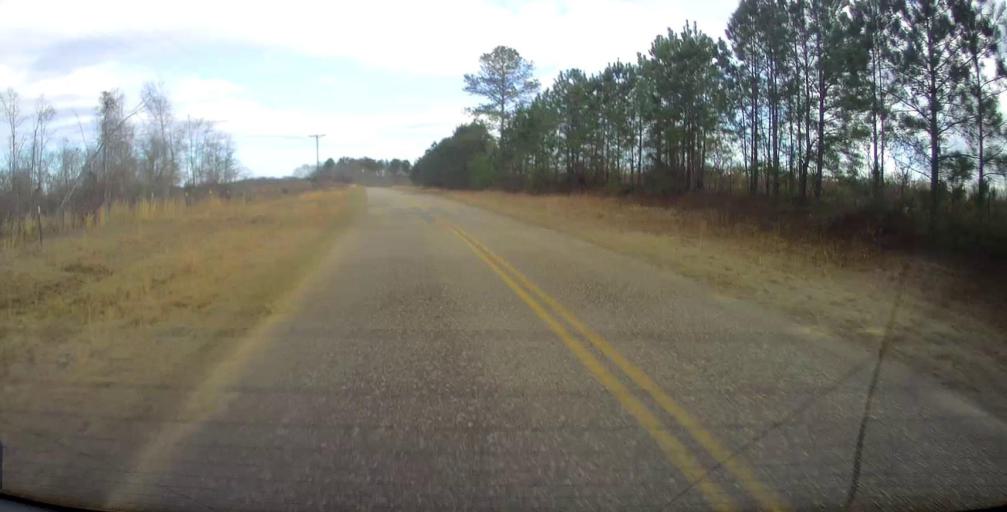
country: US
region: Georgia
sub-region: Marion County
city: Buena Vista
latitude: 32.4190
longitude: -84.4147
